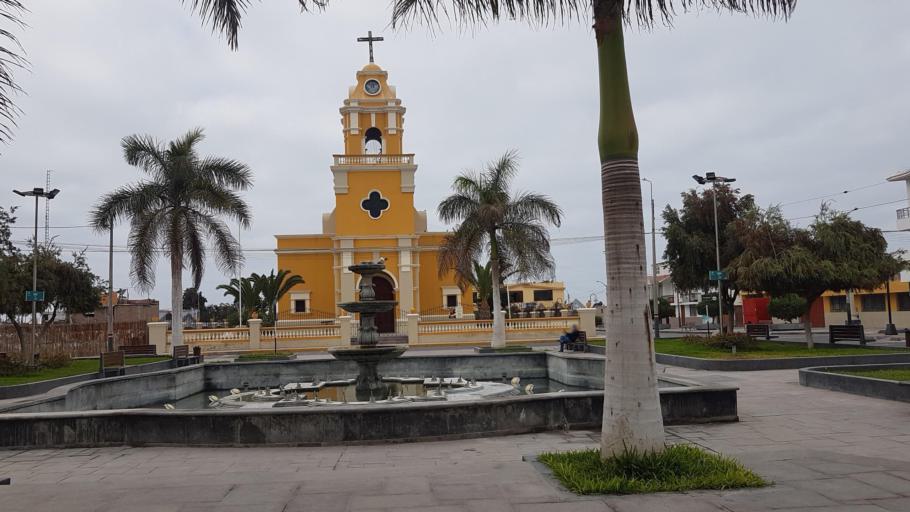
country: PE
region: Arequipa
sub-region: Provincia de Islay
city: Punta de Bombon
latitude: -17.1722
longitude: -71.7906
